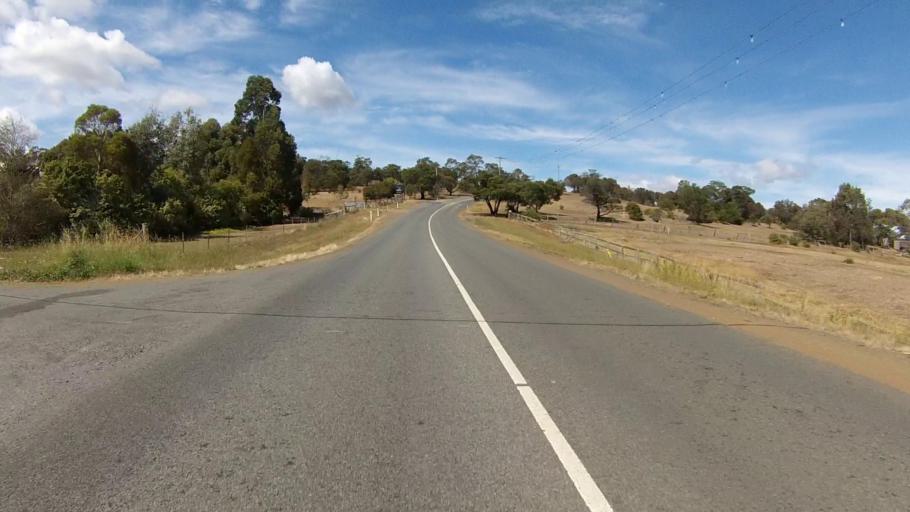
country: AU
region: Tasmania
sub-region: Brighton
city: Bridgewater
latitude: -42.7054
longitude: 147.2706
